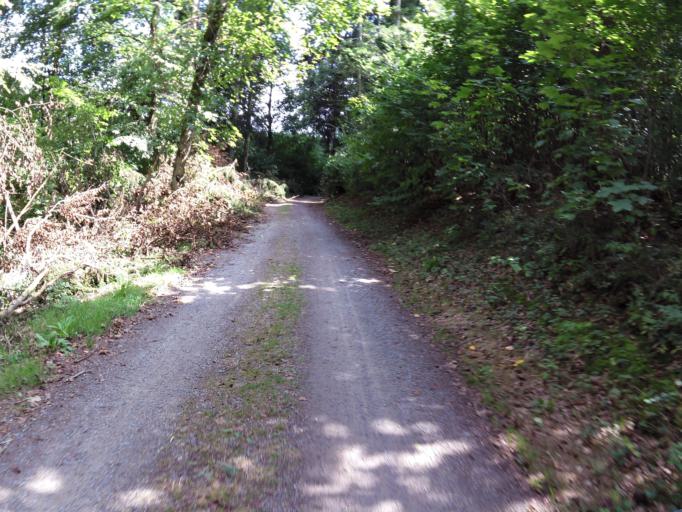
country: DE
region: Baden-Wuerttemberg
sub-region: Freiburg Region
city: Sulz am Neckar
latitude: 48.3946
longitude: 8.6506
